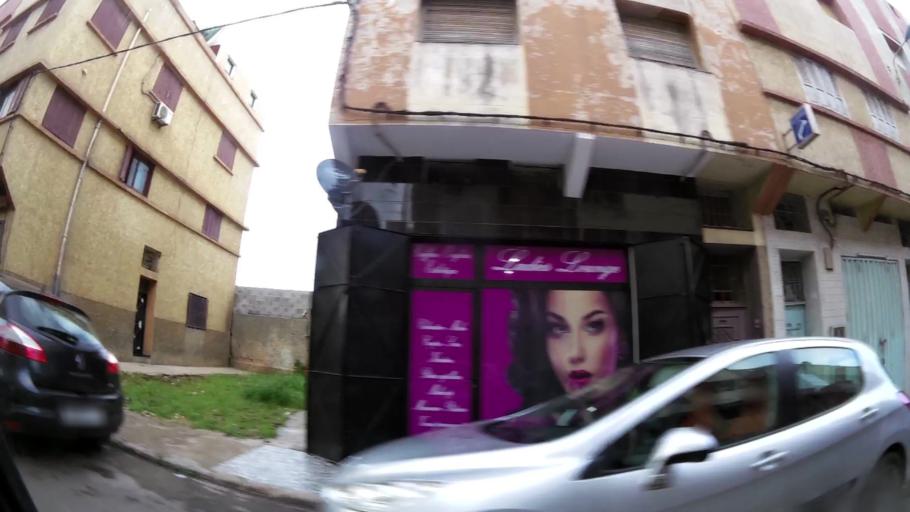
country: MA
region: Grand Casablanca
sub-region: Mohammedia
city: Mohammedia
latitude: 33.6830
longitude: -7.3919
